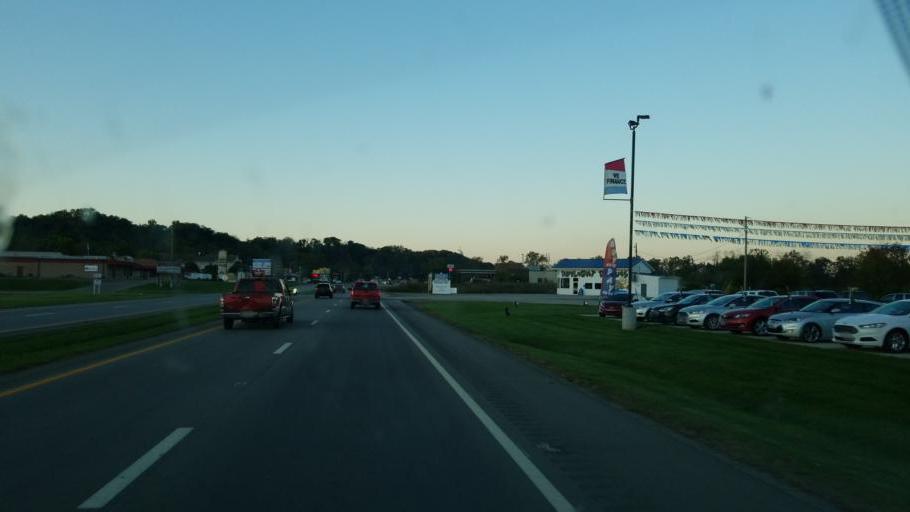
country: US
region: Ohio
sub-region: Pike County
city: Waverly
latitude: 39.1121
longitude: -82.9970
